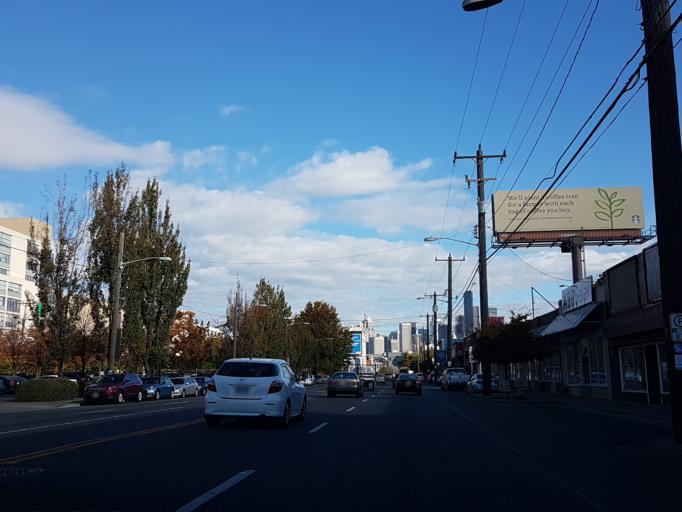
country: US
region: Washington
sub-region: King County
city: Seattle
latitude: 47.5802
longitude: -122.3341
